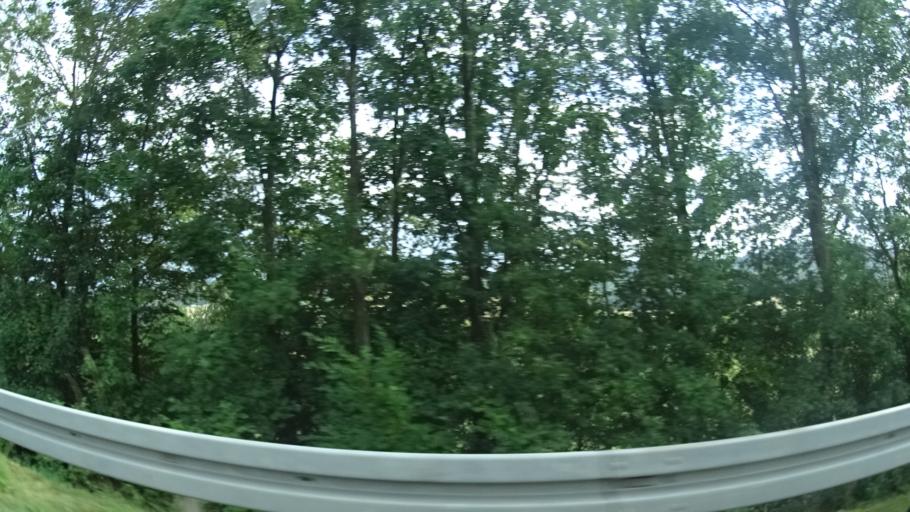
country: DE
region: Hesse
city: Grebenau
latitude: 50.7728
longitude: 9.5344
